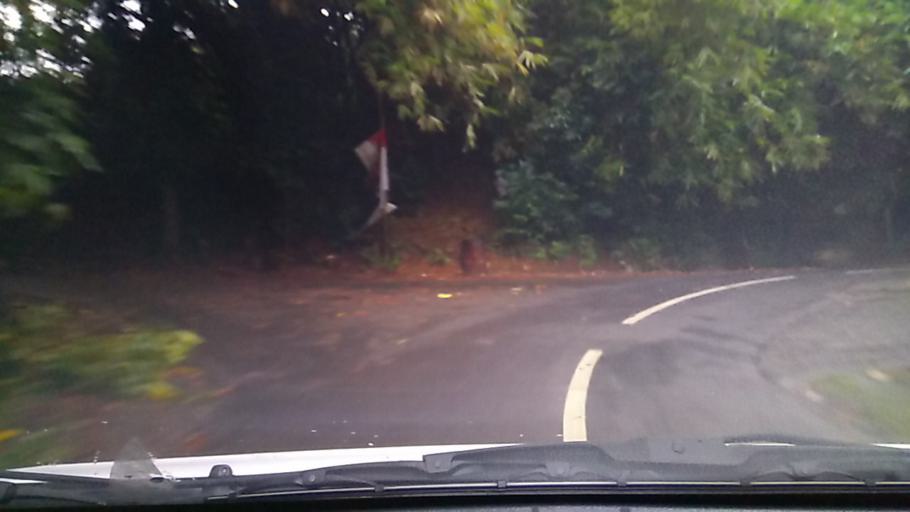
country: ID
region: Bali
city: Tiyingtali Kelod
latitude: -8.4048
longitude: 115.6197
